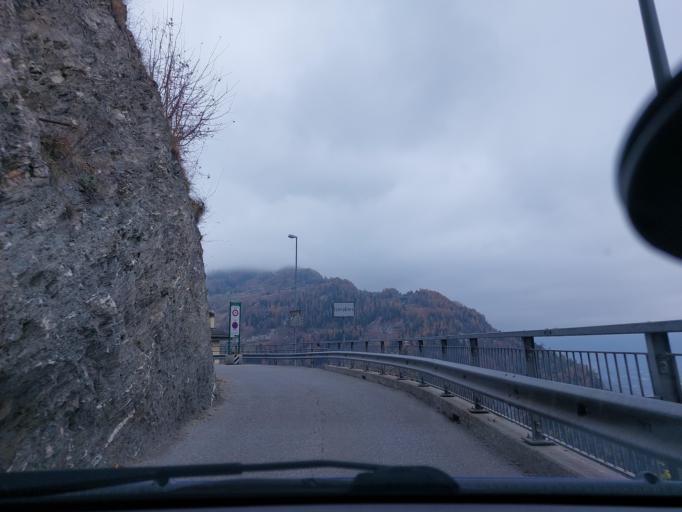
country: CH
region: Valais
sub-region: Martigny District
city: Riddes
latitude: 46.1686
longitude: 7.2431
